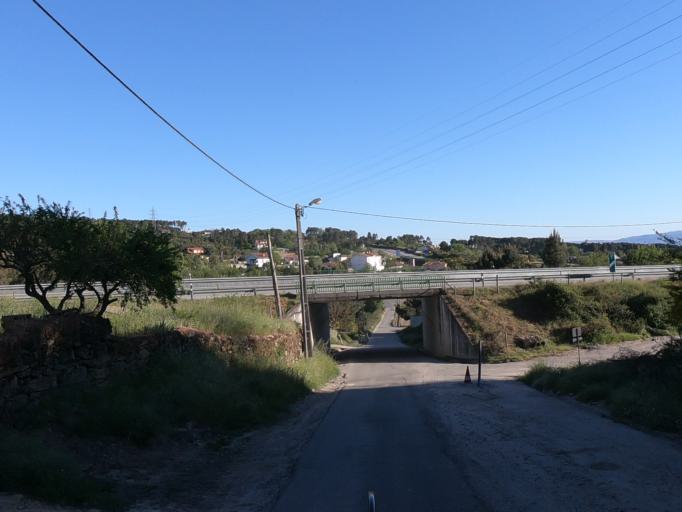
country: PT
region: Vila Real
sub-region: Vila Real
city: Vila Real
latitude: 41.3255
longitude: -7.6942
